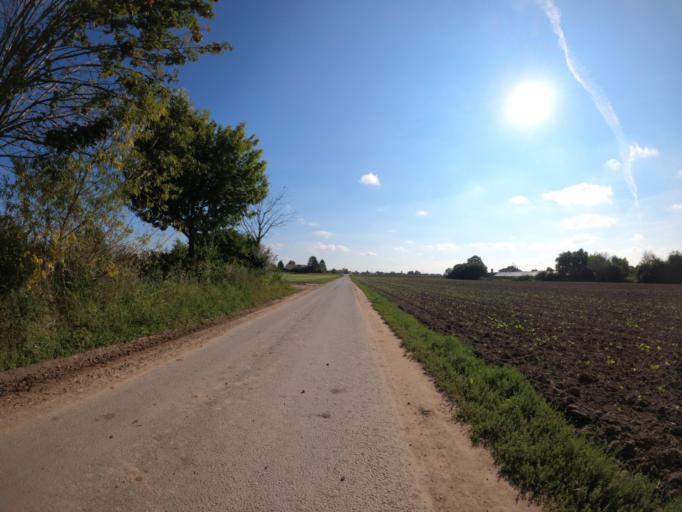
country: DE
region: Rheinland-Pfalz
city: Lambsheim
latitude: 49.5064
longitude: 8.2790
